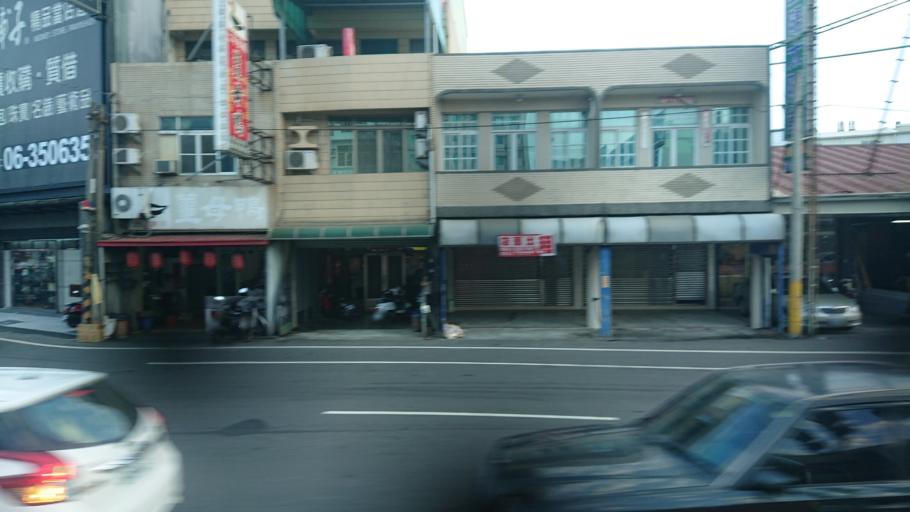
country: TW
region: Taiwan
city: Xinying
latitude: 23.1849
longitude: 120.2405
